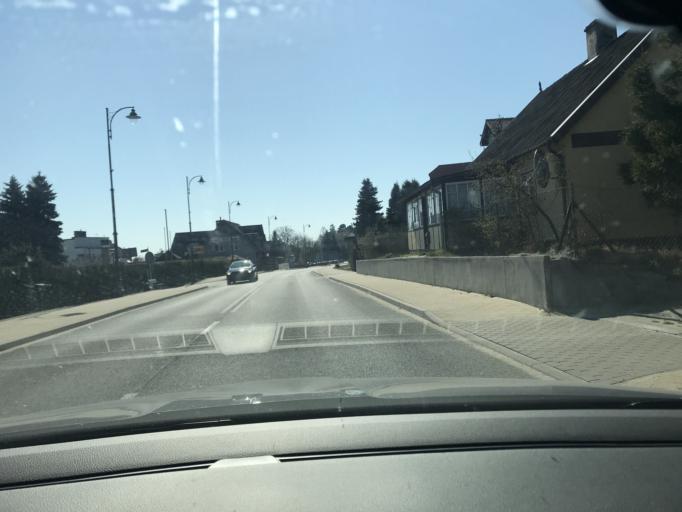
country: PL
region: Pomeranian Voivodeship
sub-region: Powiat nowodworski
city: Krynica Morska
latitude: 54.3742
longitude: 19.4229
